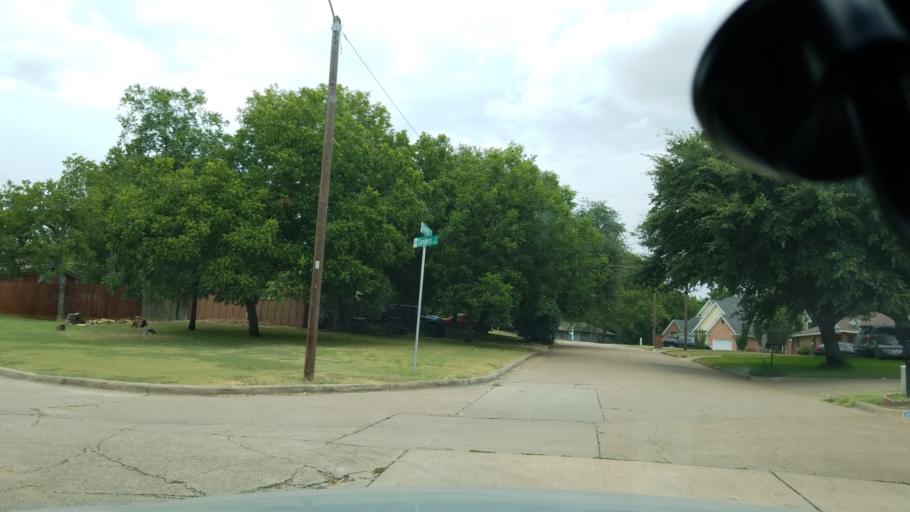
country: US
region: Texas
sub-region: Dallas County
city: Grand Prairie
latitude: 32.7354
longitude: -96.9980
